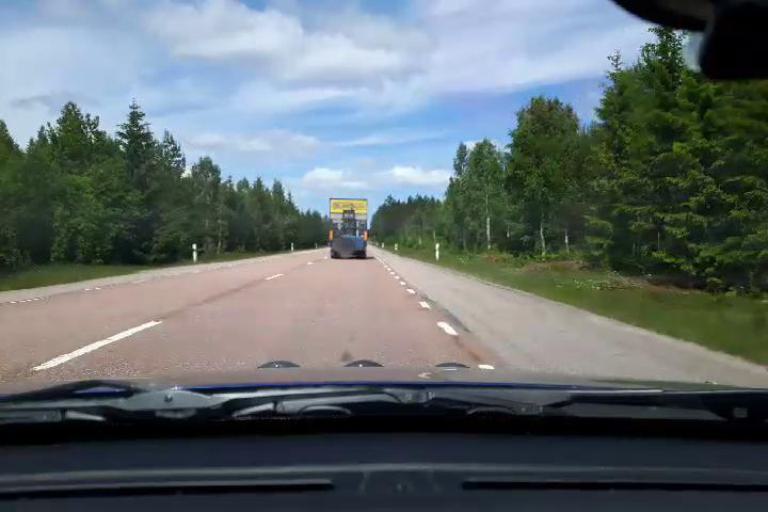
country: SE
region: Uppsala
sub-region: Osthammars Kommun
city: Bjorklinge
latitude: 60.1589
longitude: 17.4912
